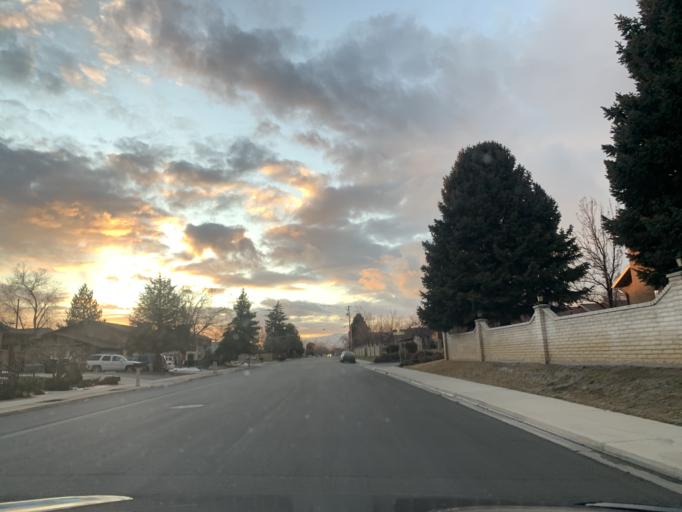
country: US
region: Utah
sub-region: Utah County
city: Provo
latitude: 40.2566
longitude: -111.6799
